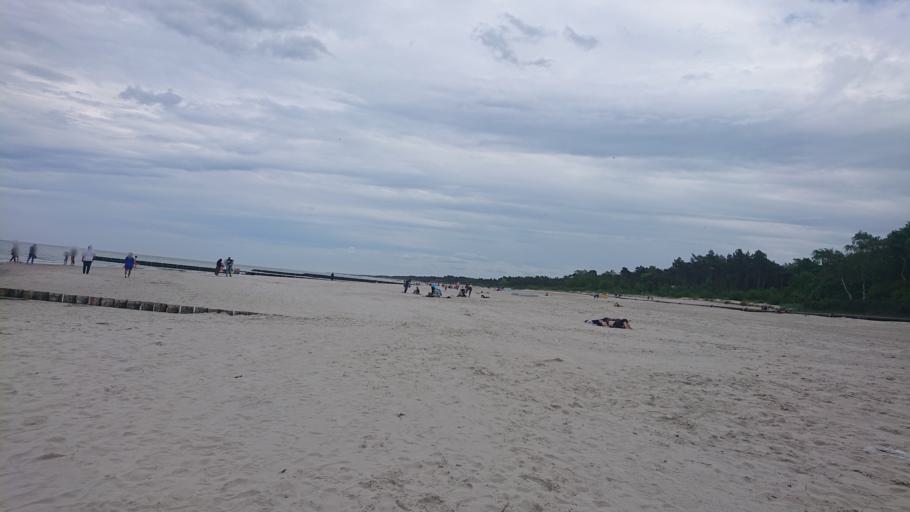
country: PL
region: Pomeranian Voivodeship
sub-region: Powiat leborski
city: Leba
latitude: 54.7688
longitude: 17.5622
